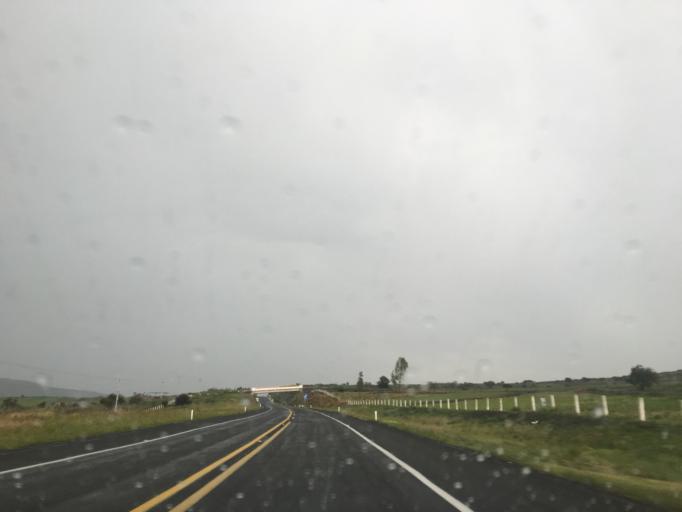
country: MX
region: Michoacan
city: Alvaro Obregon
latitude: 19.8091
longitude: -101.0166
